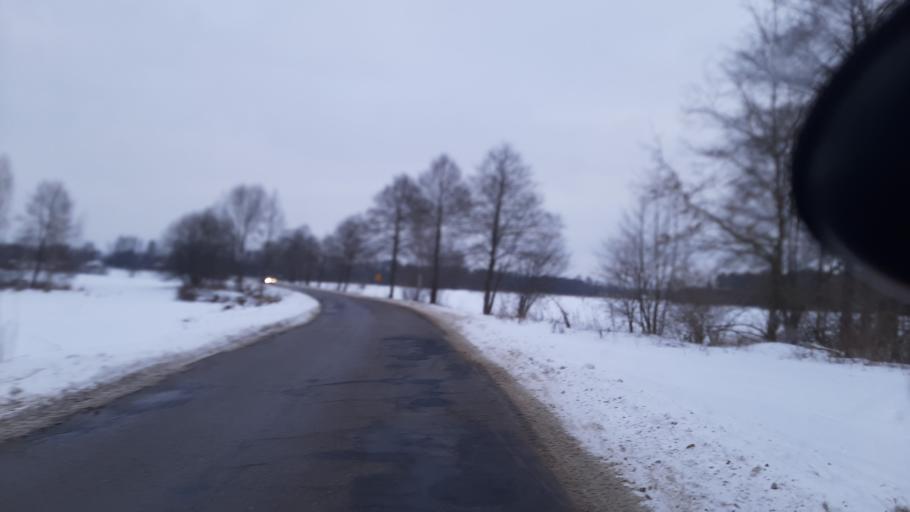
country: PL
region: Lublin Voivodeship
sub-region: Powiat pulawski
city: Kurow
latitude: 51.4157
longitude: 22.2012
